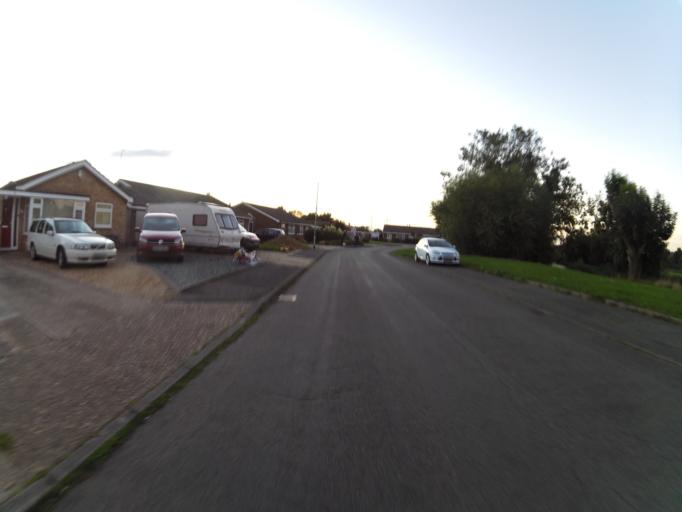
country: GB
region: England
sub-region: Suffolk
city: Bramford
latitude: 52.0806
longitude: 1.1002
